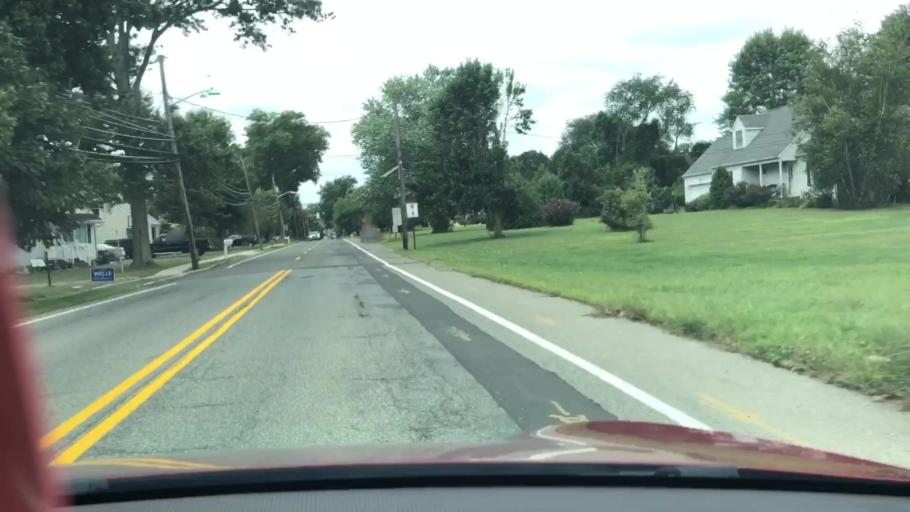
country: US
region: New Jersey
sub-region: Monmouth County
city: Allentown
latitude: 40.1768
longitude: -74.5774
